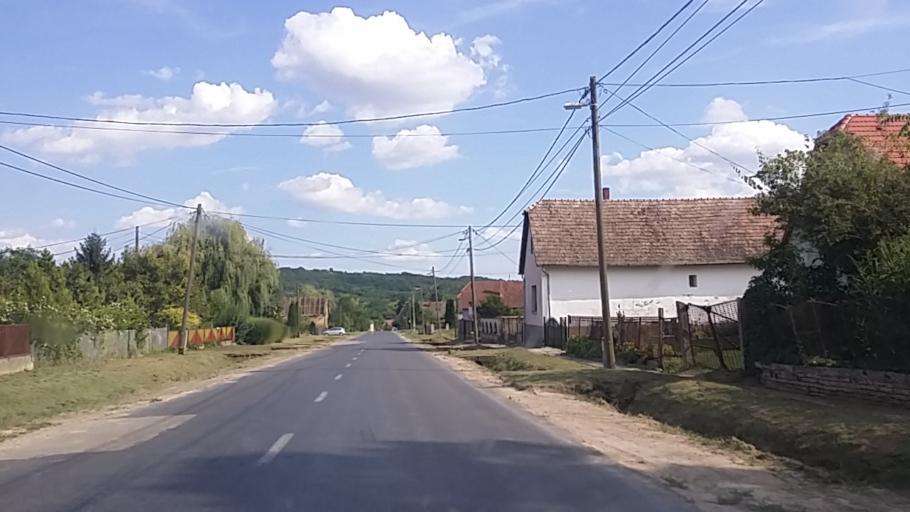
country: HU
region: Tolna
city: Zomba
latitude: 46.5057
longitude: 18.5598
